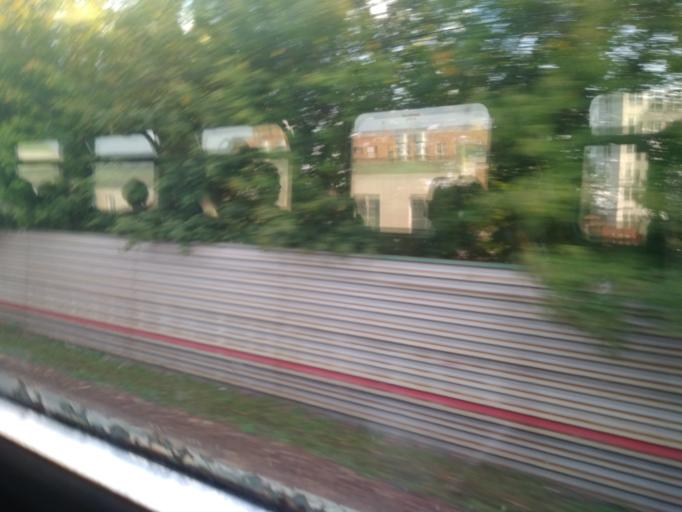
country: RU
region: Moscow
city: Ryazanskiy
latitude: 55.7388
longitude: 37.7505
